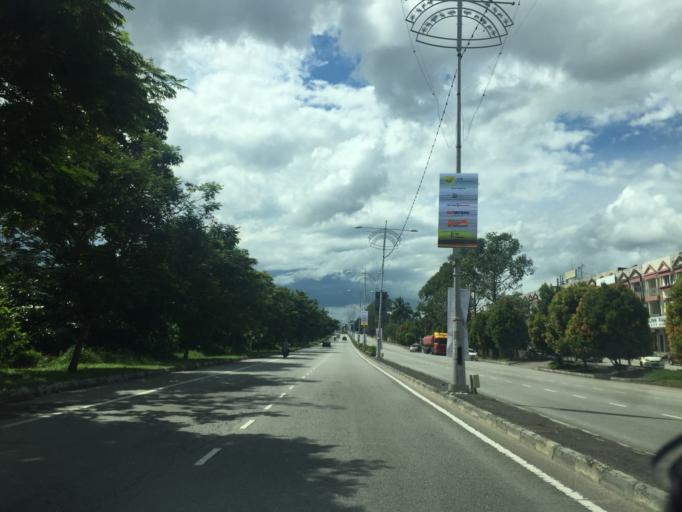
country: MY
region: Negeri Sembilan
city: Seremban
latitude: 2.7222
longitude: 101.9326
